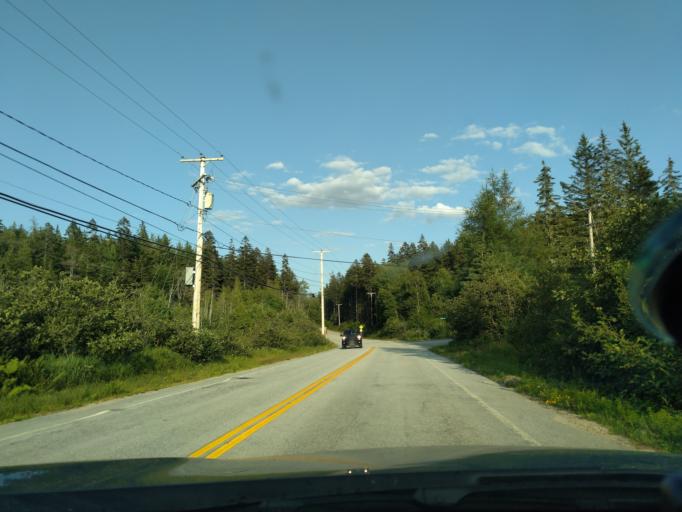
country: US
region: Maine
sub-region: Hancock County
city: Gouldsboro
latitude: 44.3941
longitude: -68.0746
